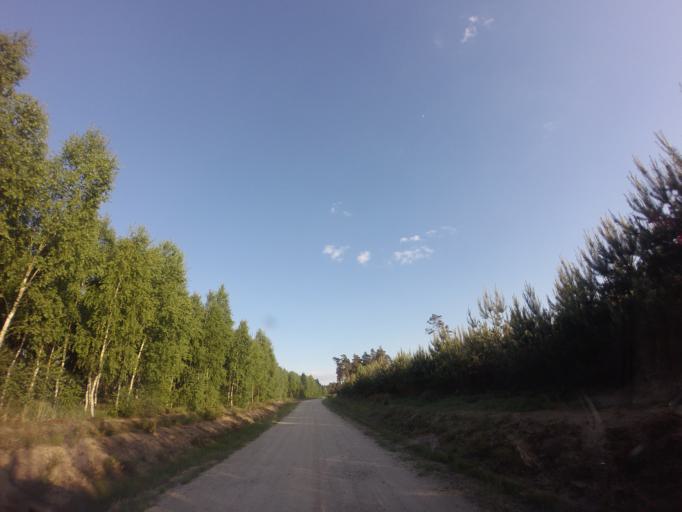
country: PL
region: West Pomeranian Voivodeship
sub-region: Powiat choszczenski
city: Drawno
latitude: 53.1411
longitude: 15.7327
